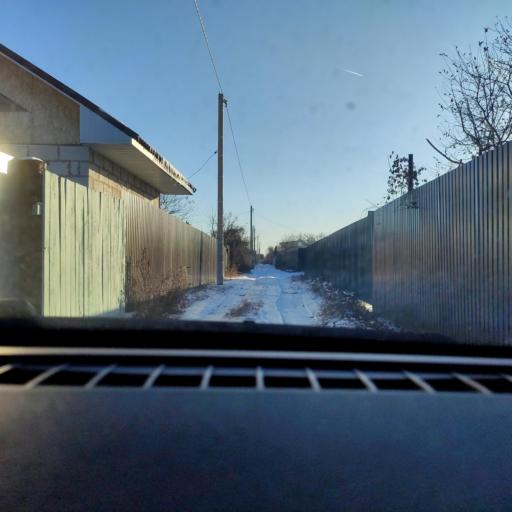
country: RU
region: Voronezj
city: Maslovka
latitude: 51.6060
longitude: 39.2742
